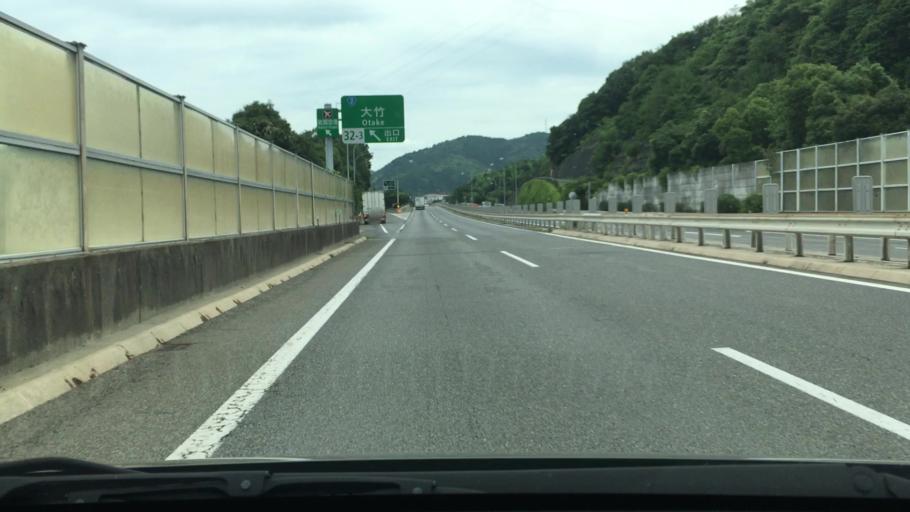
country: JP
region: Yamaguchi
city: Otake
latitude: 34.2477
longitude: 132.2187
